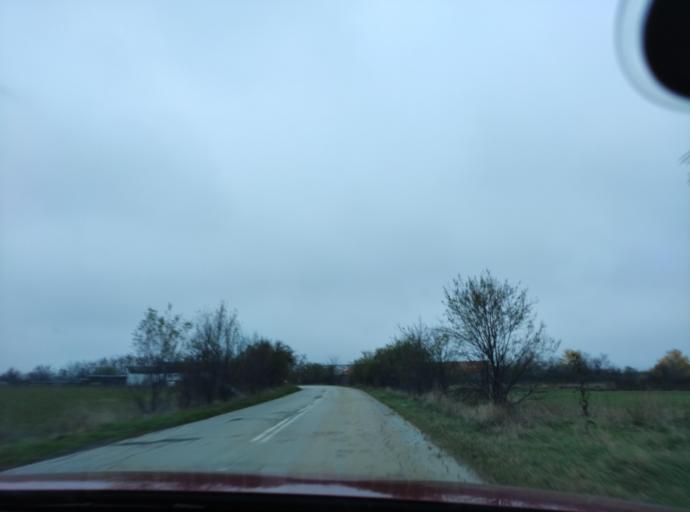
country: BG
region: Lovech
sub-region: Obshtina Yablanitsa
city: Yablanitsa
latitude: 43.0770
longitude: 24.0772
